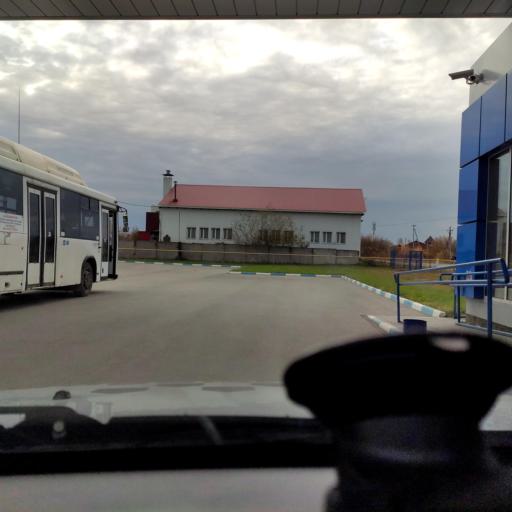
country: RU
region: Perm
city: Froly
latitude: 57.9579
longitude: 56.2865
